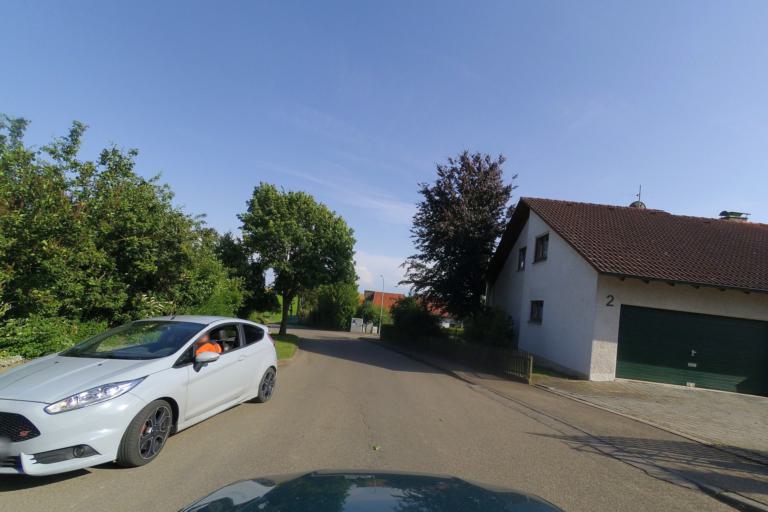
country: DE
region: Baden-Wuerttemberg
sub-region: Regierungsbezirk Stuttgart
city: Sontheim an der Brenz
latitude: 48.5713
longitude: 10.2741
